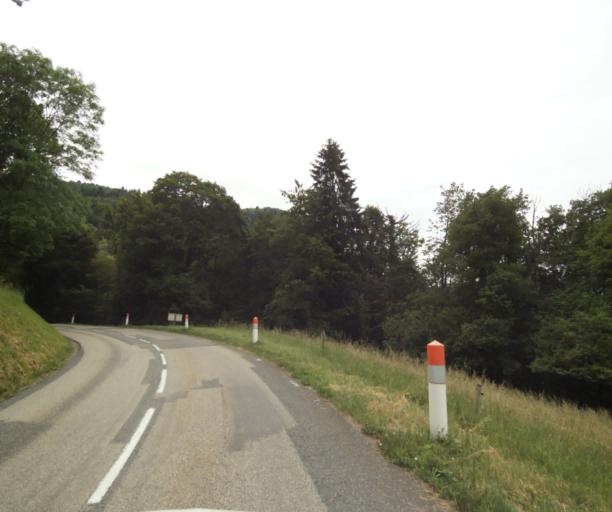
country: FR
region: Rhone-Alpes
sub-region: Departement de la Haute-Savoie
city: Perrignier
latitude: 46.2935
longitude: 6.4644
